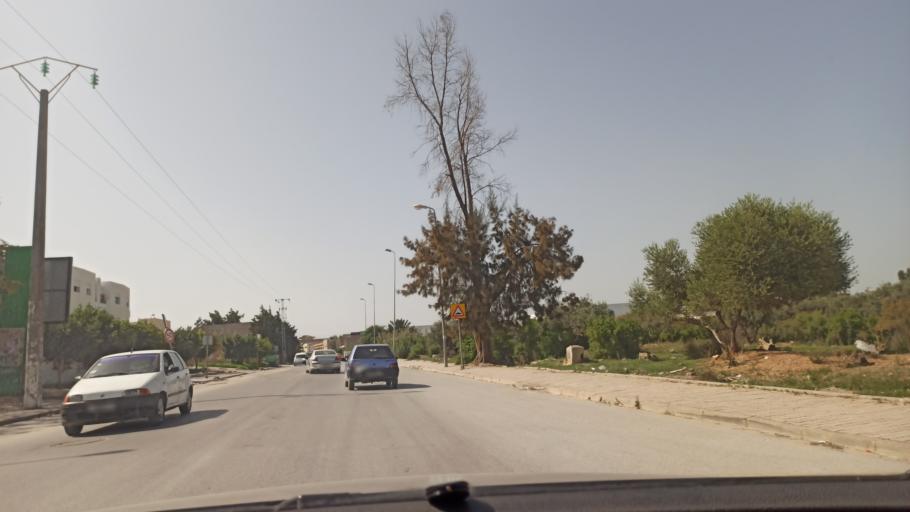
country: TN
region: Manouba
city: Manouba
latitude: 36.7588
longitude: 10.1053
